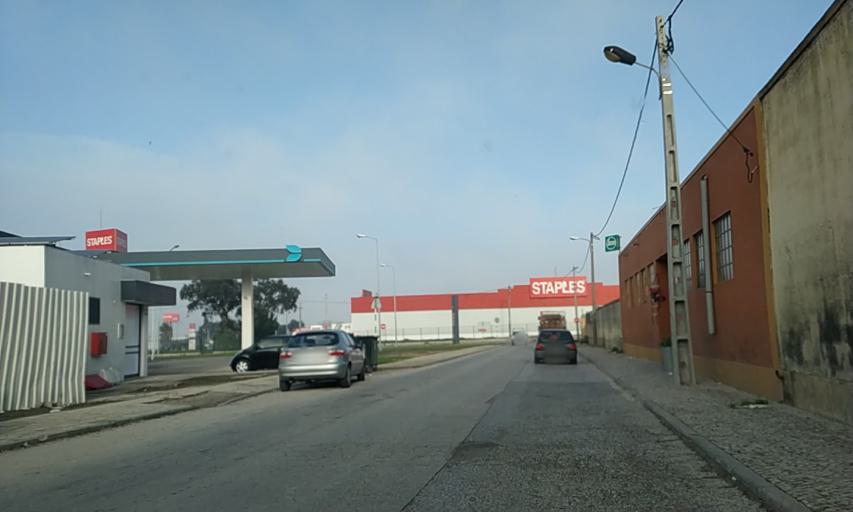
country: PT
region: Setubal
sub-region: Montijo
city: Montijo
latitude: 38.6881
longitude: -8.9446
